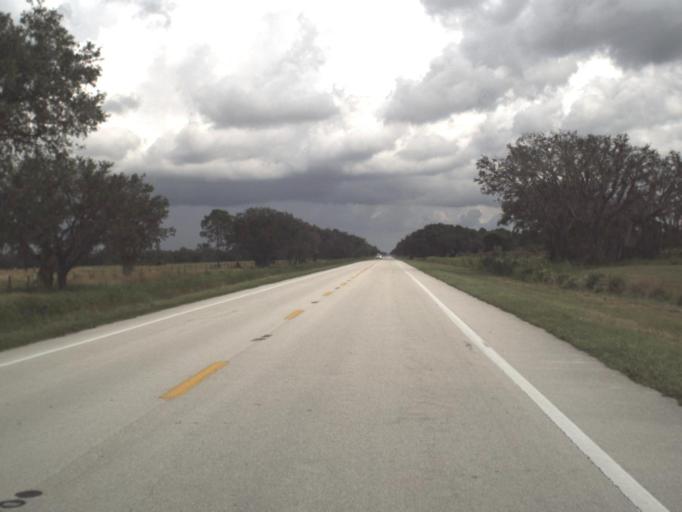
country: US
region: Florida
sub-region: Hendry County
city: Port LaBelle
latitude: 26.8330
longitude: -81.3951
